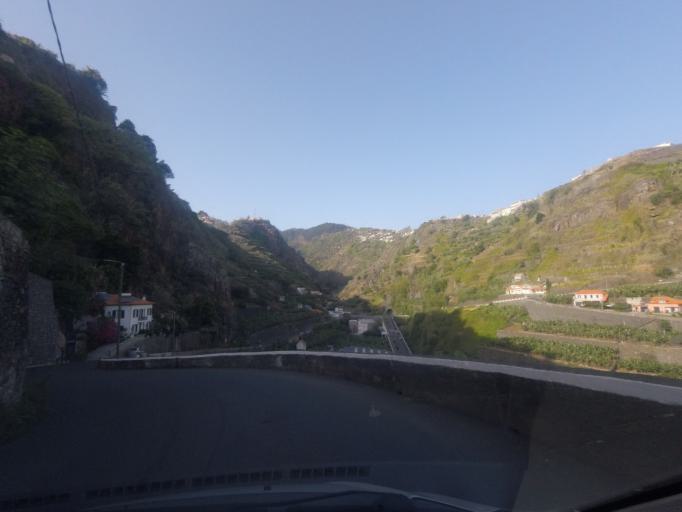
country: PT
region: Madeira
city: Ponta do Sol
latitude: 32.6836
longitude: -17.1015
